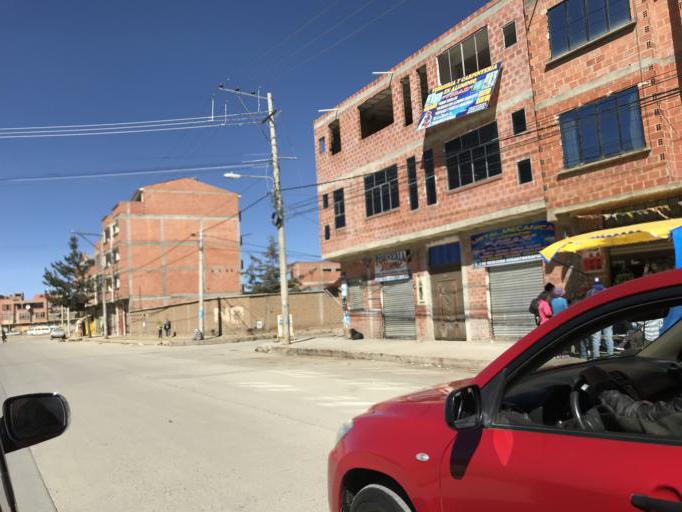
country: BO
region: La Paz
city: La Paz
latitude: -16.4863
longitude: -68.2031
